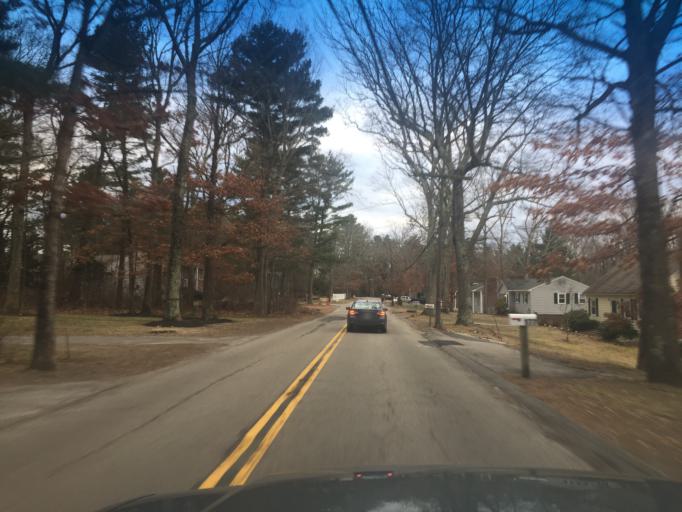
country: US
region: Massachusetts
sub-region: Norfolk County
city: Medway
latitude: 42.1506
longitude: -71.3815
